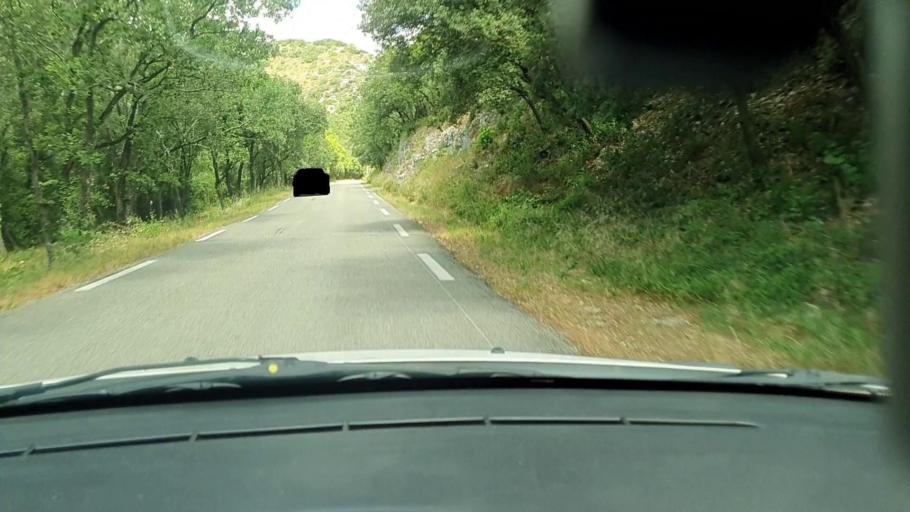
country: FR
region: Languedoc-Roussillon
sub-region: Departement du Gard
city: Cabrieres
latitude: 43.9399
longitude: 4.4783
